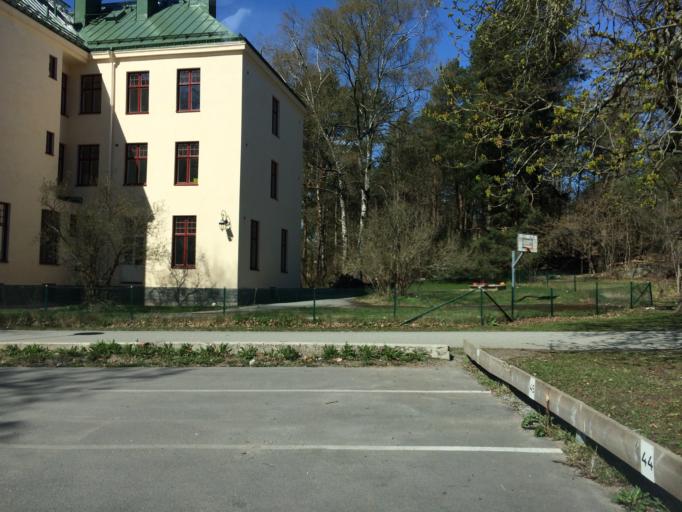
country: SE
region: Stockholm
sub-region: Huddinge Kommun
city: Segeltorp
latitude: 59.2819
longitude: 17.9747
